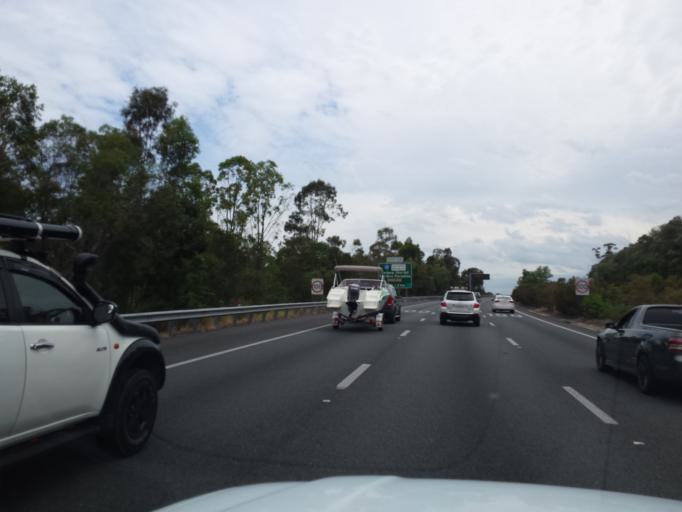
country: AU
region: Queensland
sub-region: Gold Coast
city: Nerang
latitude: -27.9669
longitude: 153.3467
